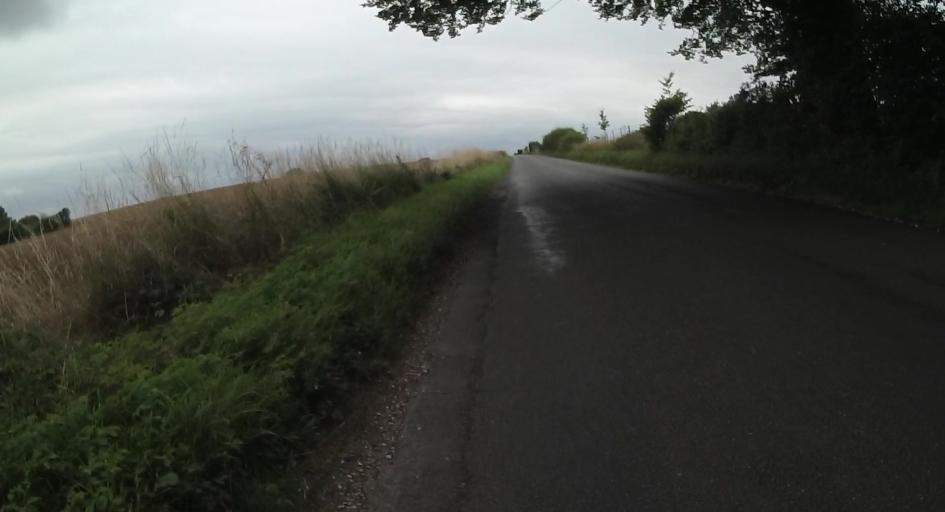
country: GB
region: England
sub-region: Hampshire
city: Bishops Waltham
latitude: 51.0292
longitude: -1.2084
